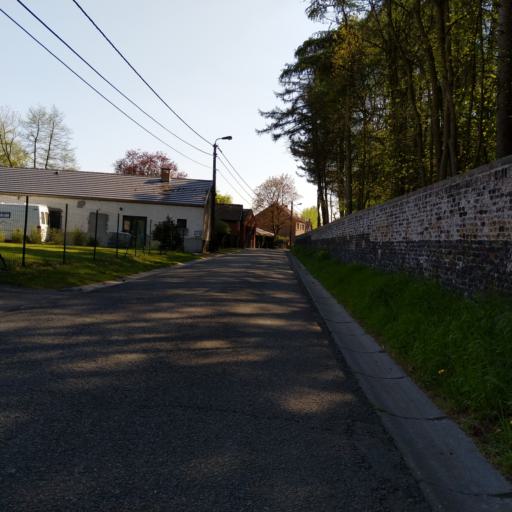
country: BE
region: Wallonia
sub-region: Province du Hainaut
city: Jurbise
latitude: 50.5123
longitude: 3.9333
